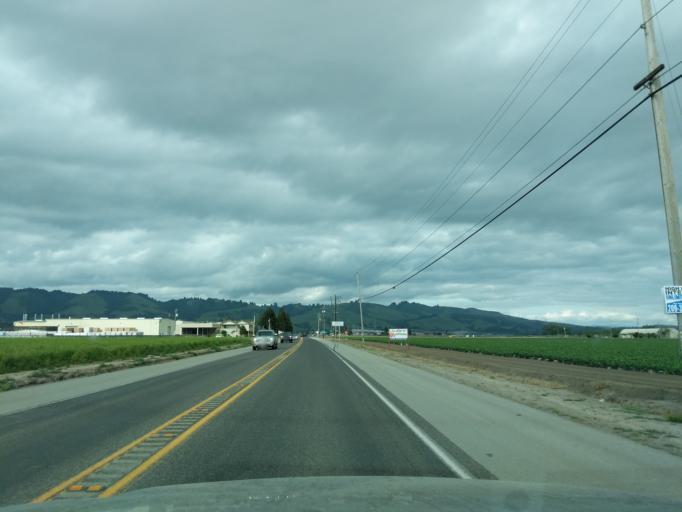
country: US
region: California
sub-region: Monterey County
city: Pajaro
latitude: 36.9154
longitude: -121.7362
